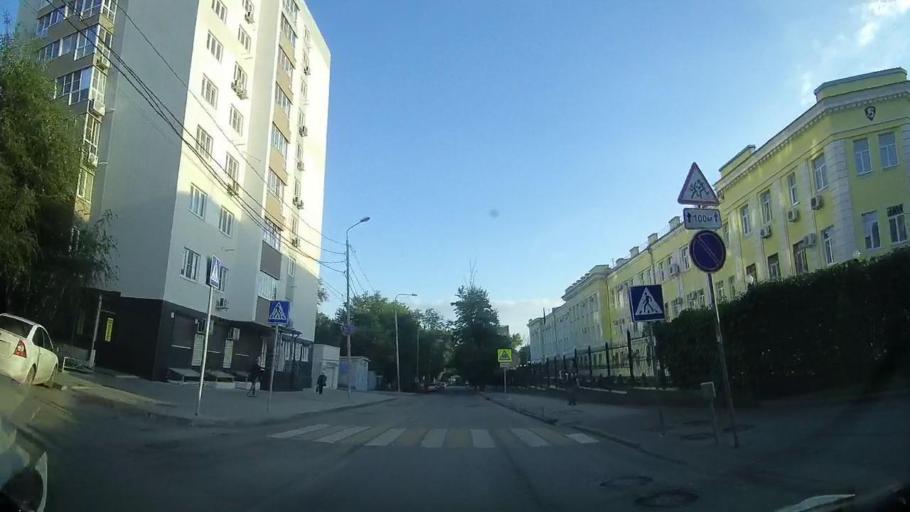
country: RU
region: Rostov
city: Rostov-na-Donu
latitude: 47.2368
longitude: 39.6944
